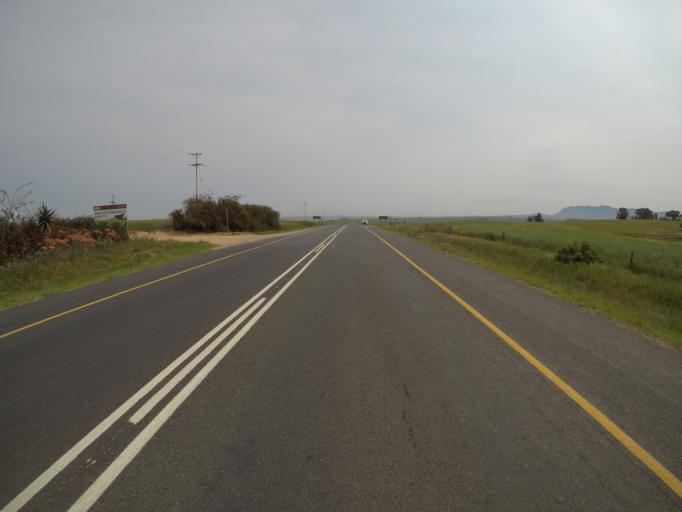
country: ZA
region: Western Cape
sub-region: West Coast District Municipality
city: Malmesbury
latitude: -33.5029
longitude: 18.8366
